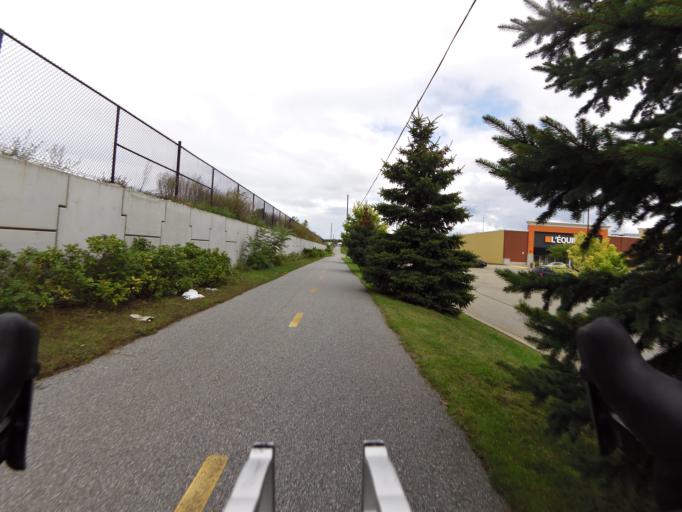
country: CA
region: Quebec
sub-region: Outaouais
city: Gatineau
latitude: 45.4675
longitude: -75.7187
